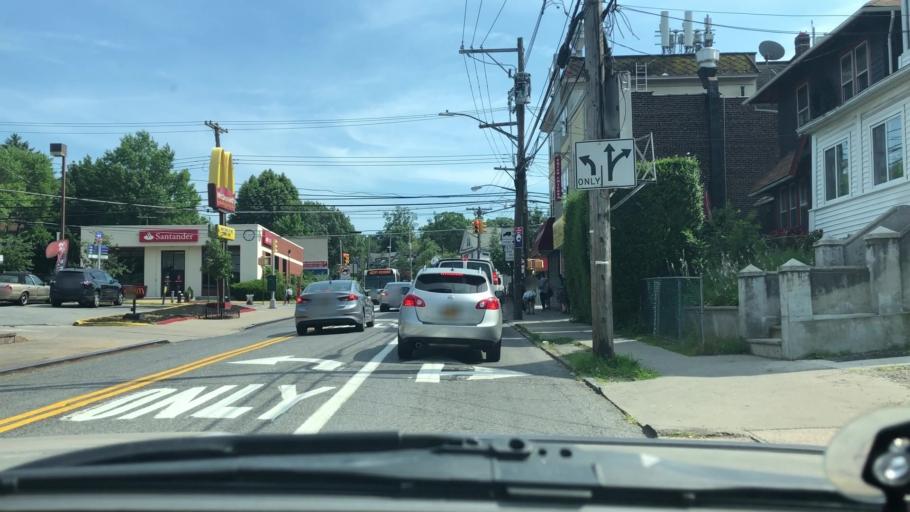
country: US
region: New Jersey
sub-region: Hudson County
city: Bayonne
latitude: 40.6294
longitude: -74.1163
